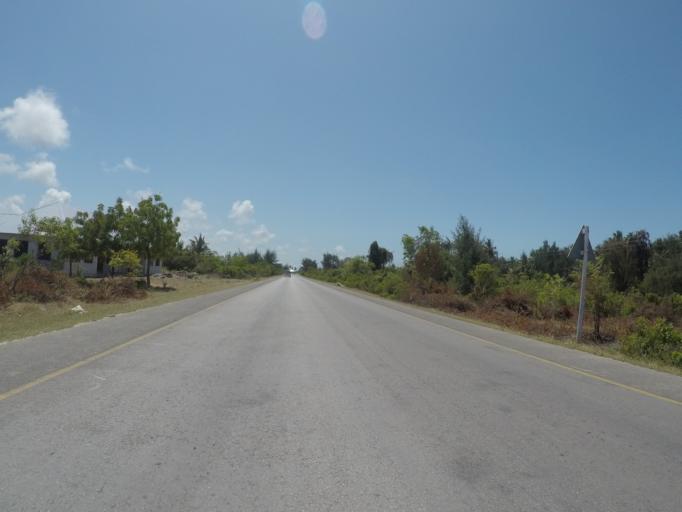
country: TZ
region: Zanzibar Central/South
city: Nganane
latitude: -6.3222
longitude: 39.5447
